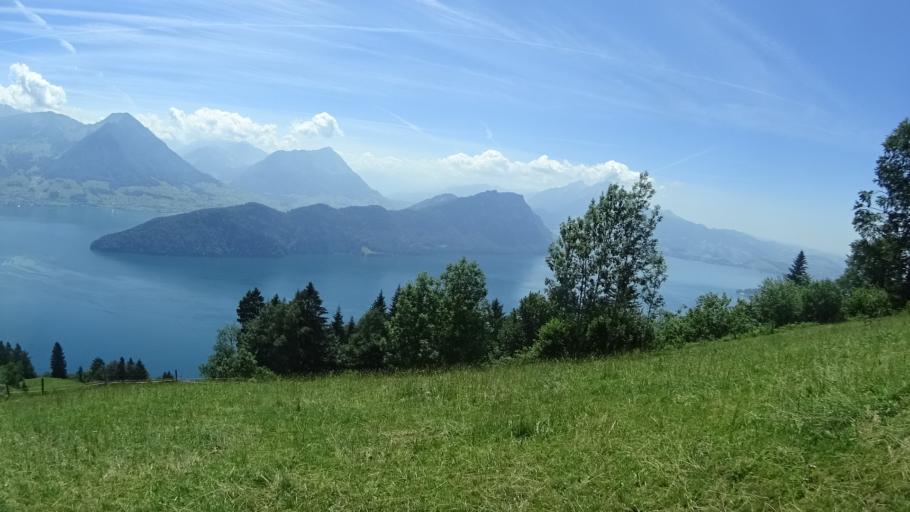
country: CH
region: Lucerne
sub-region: Lucerne-Land District
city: Vitznau
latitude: 47.0294
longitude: 8.4800
